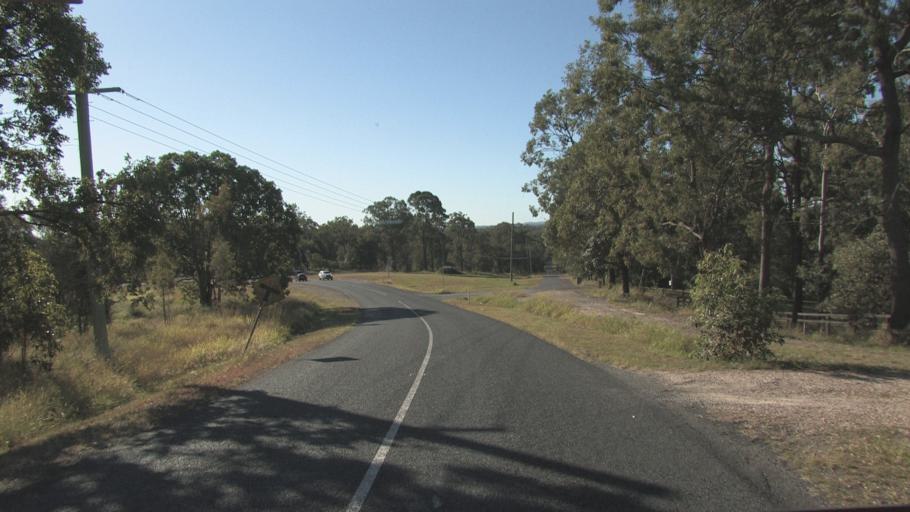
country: AU
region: Queensland
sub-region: Logan
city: Logan Reserve
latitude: -27.7259
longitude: 153.1053
